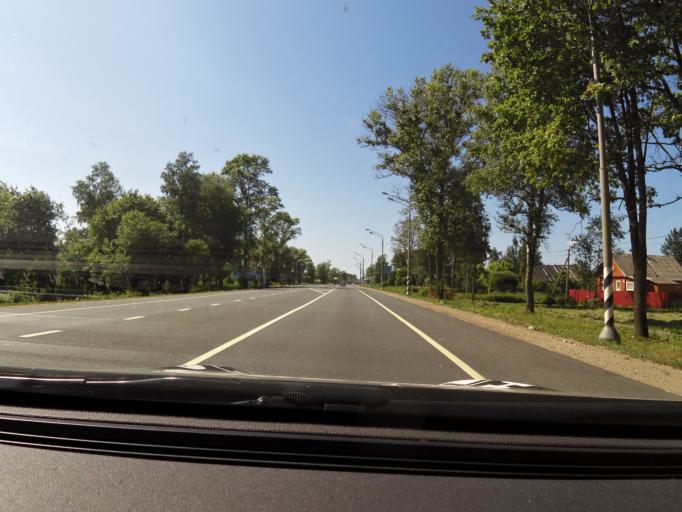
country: RU
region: Novgorod
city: Kresttsy
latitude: 58.3602
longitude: 32.2210
